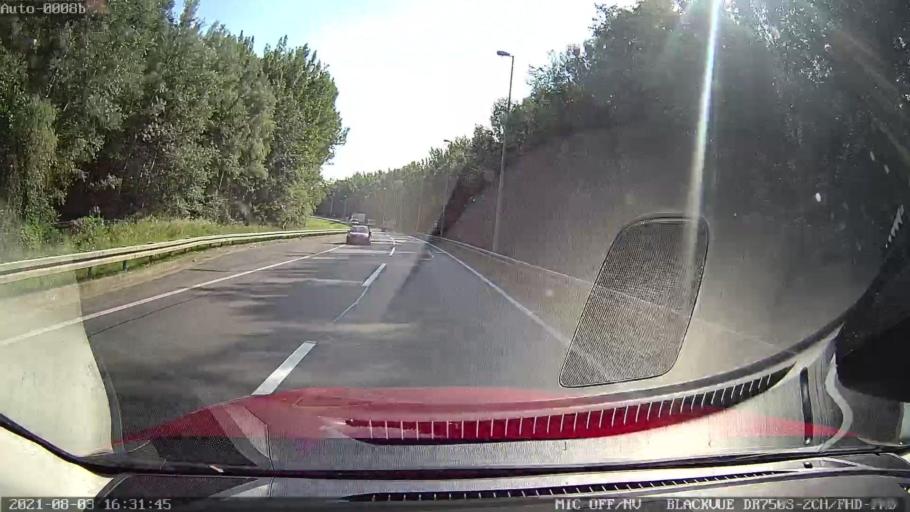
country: HR
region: Osjecko-Baranjska
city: Visnjevac
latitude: 45.5700
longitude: 18.6329
